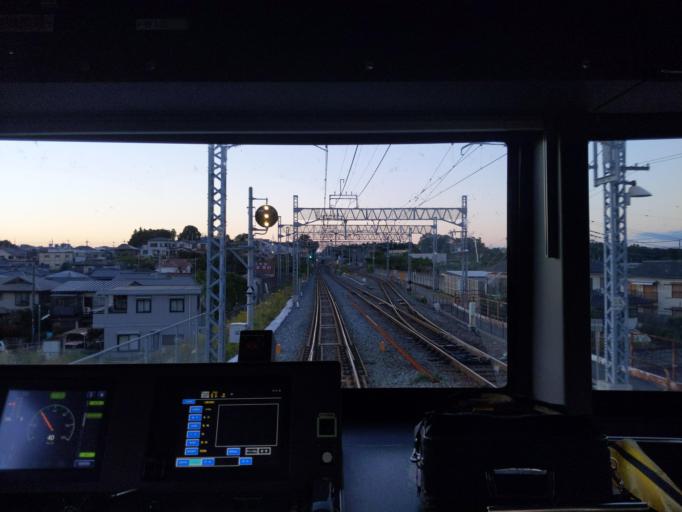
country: JP
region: Chiba
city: Kashiwa
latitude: 35.8114
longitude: 139.9971
